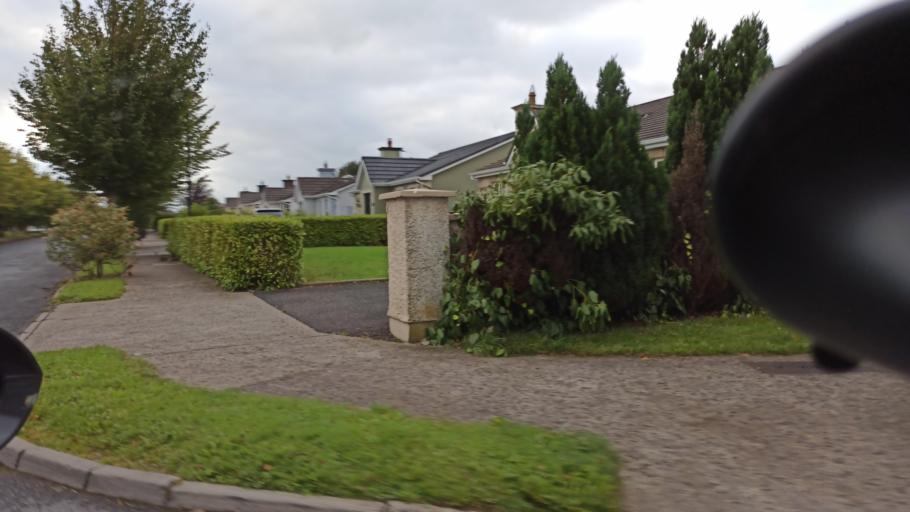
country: IE
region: Munster
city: Thurles
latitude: 52.6669
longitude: -7.8128
